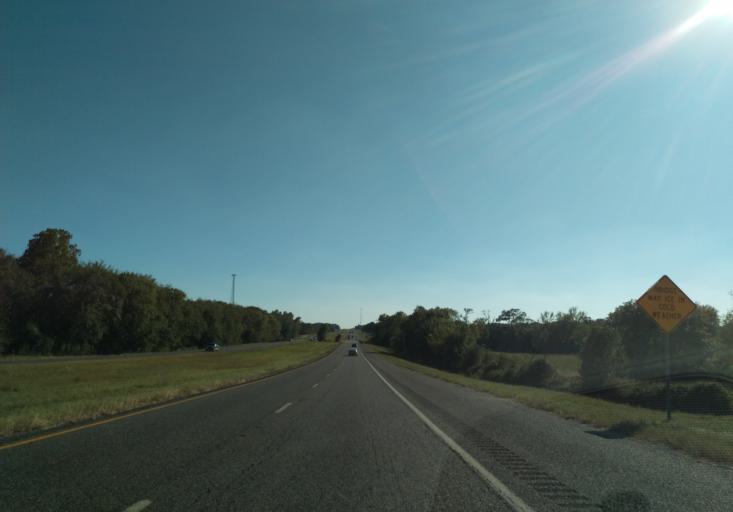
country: US
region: Texas
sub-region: Waller County
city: Hempstead
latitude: 30.1905
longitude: -96.0626
